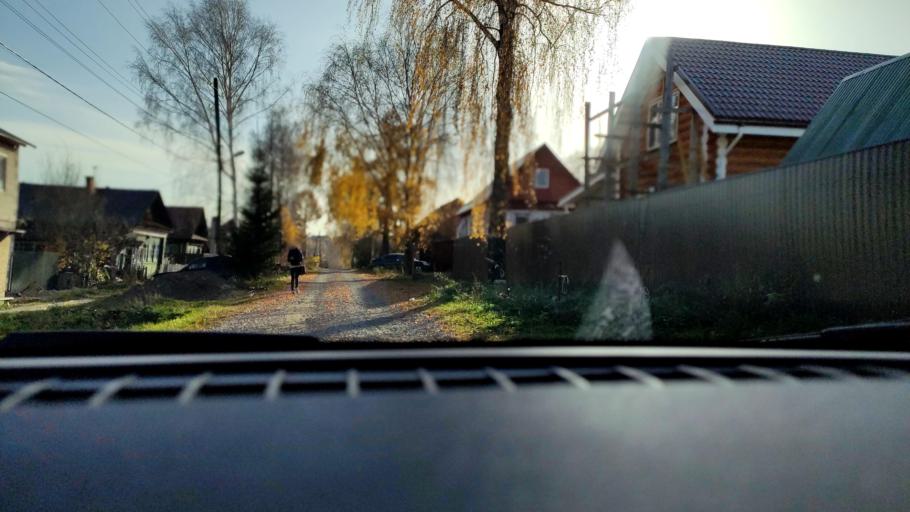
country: RU
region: Perm
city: Perm
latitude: 58.0243
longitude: 56.3157
